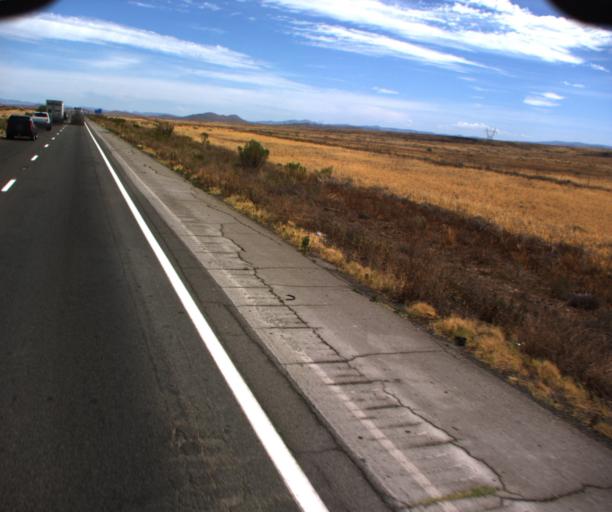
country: US
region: Arizona
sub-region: Yavapai County
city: Black Canyon City
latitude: 34.1773
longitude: -112.1348
